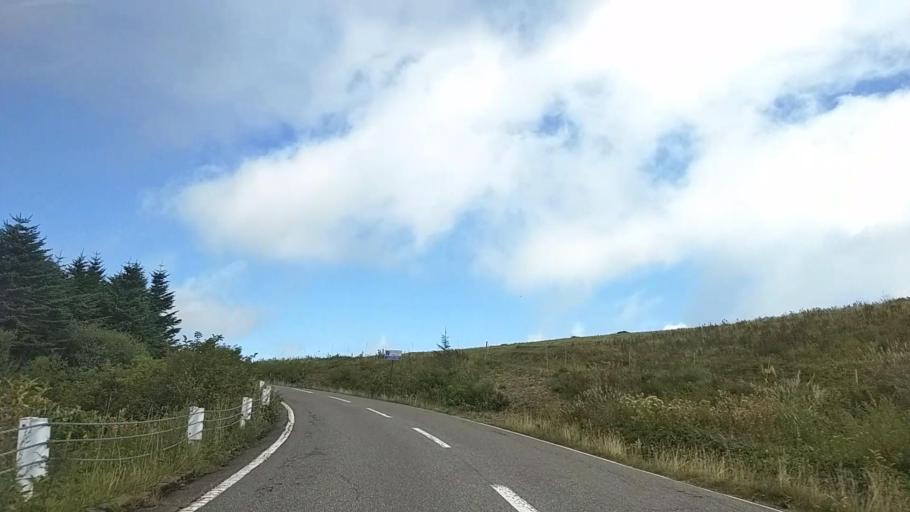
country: JP
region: Nagano
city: Suwa
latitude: 36.1024
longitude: 138.1888
